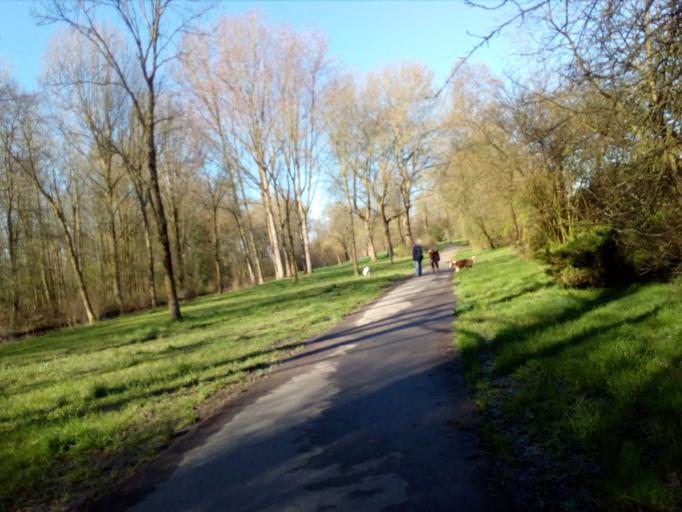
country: NL
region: South Holland
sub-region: Gemeente Zoetermeer
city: Zoetermeer
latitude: 52.0503
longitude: 4.4658
